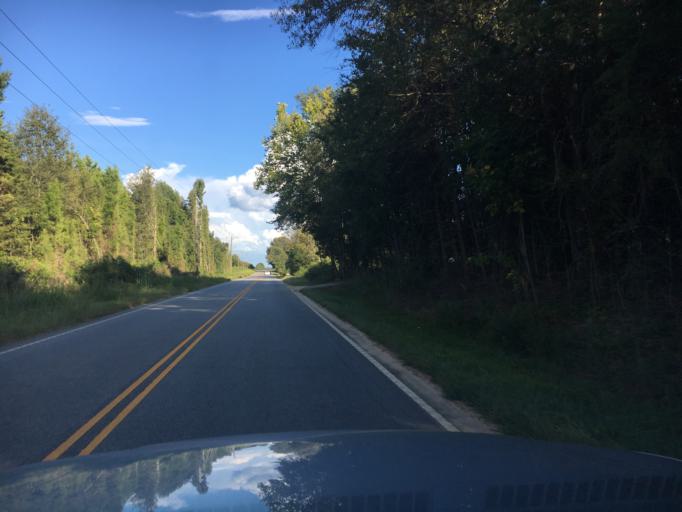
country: US
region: South Carolina
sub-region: Greenville County
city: Five Forks
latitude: 34.7980
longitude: -82.1488
